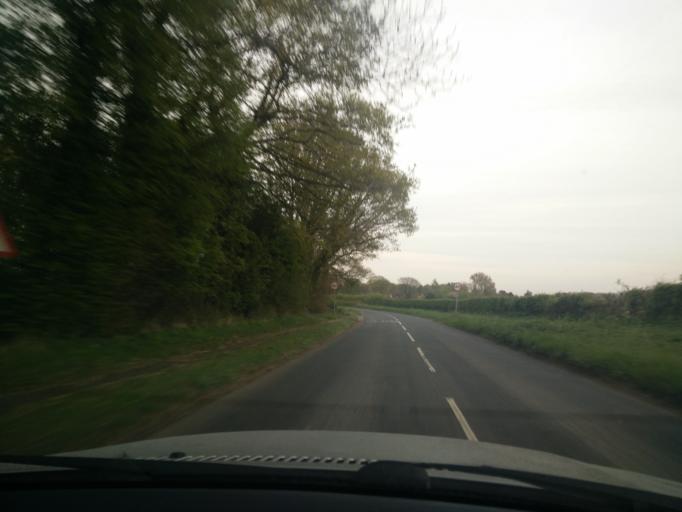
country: GB
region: England
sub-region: Buckinghamshire
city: Amersham
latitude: 51.6889
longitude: -0.6289
